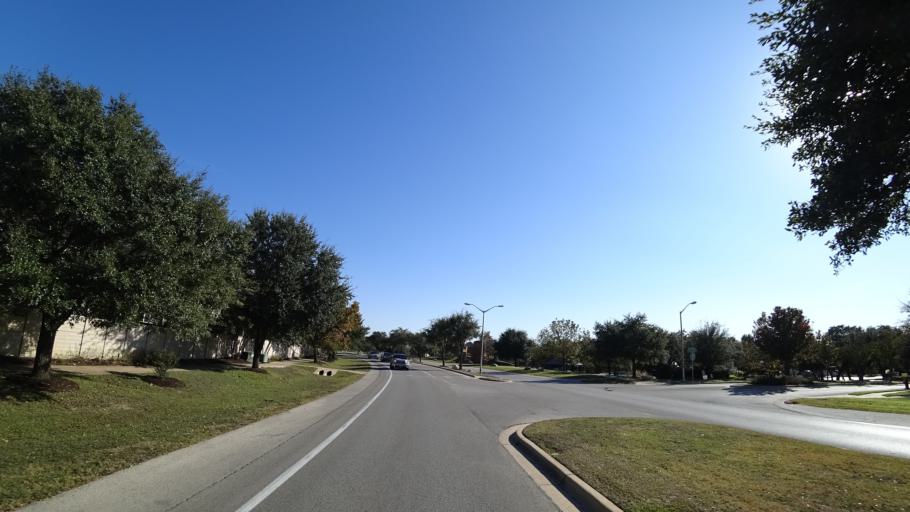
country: US
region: Texas
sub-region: Williamson County
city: Cedar Park
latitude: 30.4741
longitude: -97.8516
